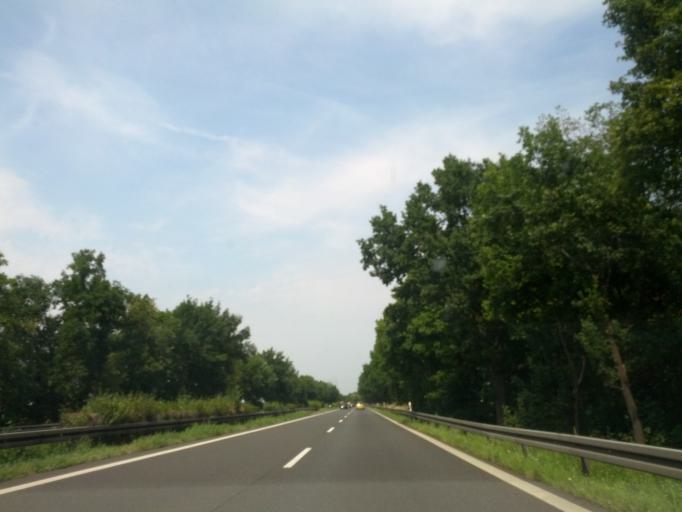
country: DE
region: Brandenburg
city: Werder
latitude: 52.4571
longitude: 12.9378
